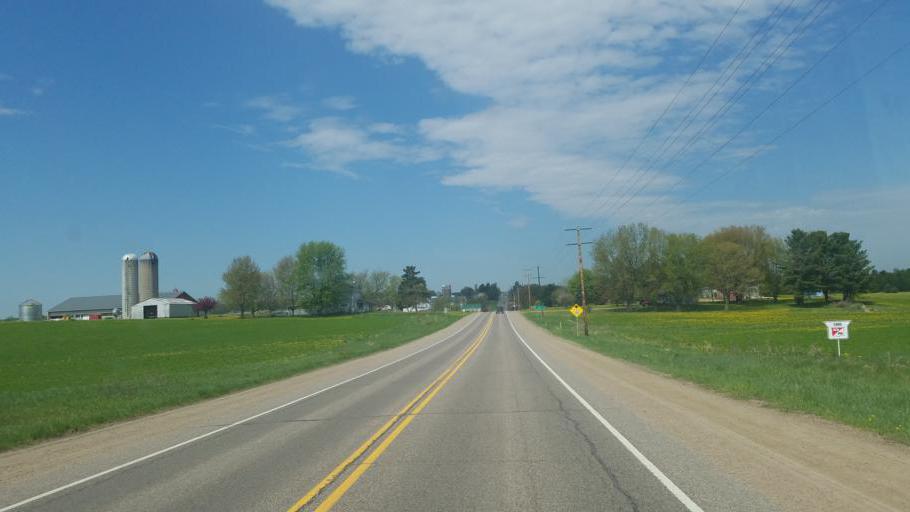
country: US
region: Wisconsin
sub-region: Clark County
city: Loyal
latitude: 44.5825
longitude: -90.3981
